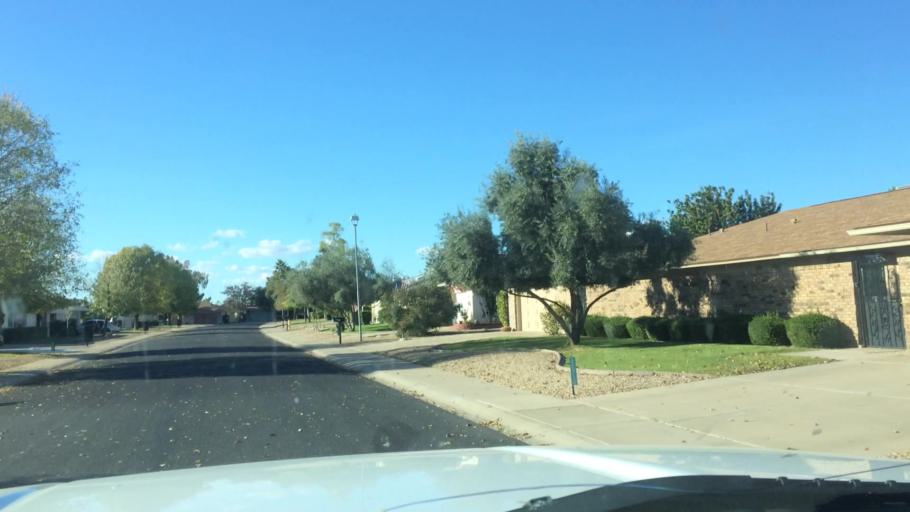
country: US
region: Arizona
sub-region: Maricopa County
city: Sun City West
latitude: 33.6531
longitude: -112.3366
